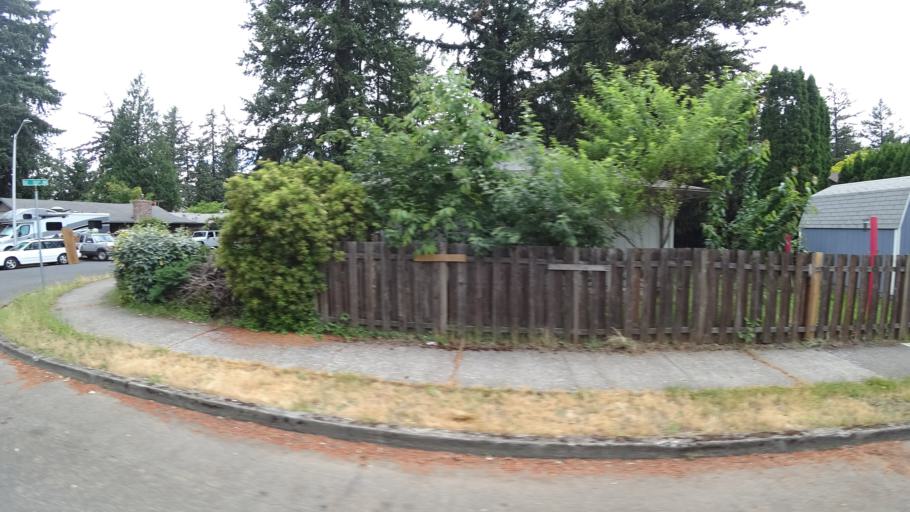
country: US
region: Oregon
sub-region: Clackamas County
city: Happy Valley
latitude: 45.4988
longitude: -122.5077
